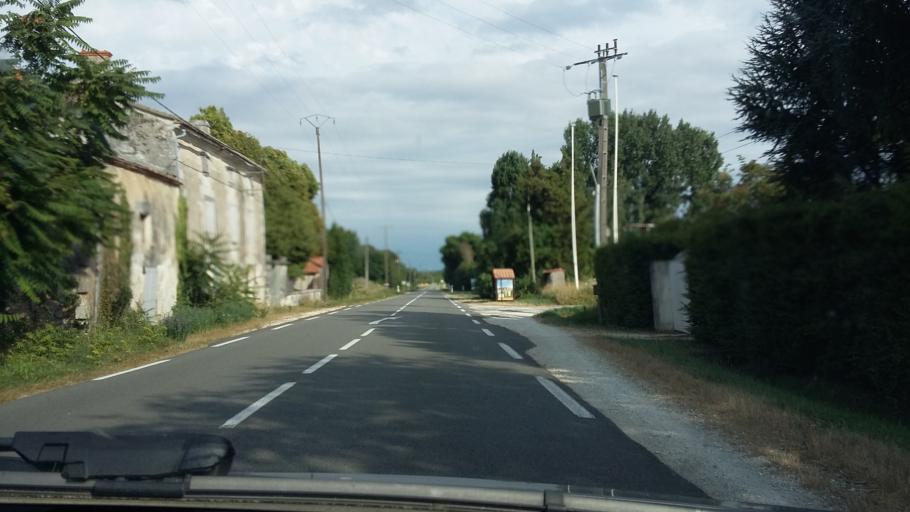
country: FR
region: Poitou-Charentes
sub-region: Departement de la Charente
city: Asnieres-sur-Nouere
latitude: 45.7076
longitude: 0.0831
